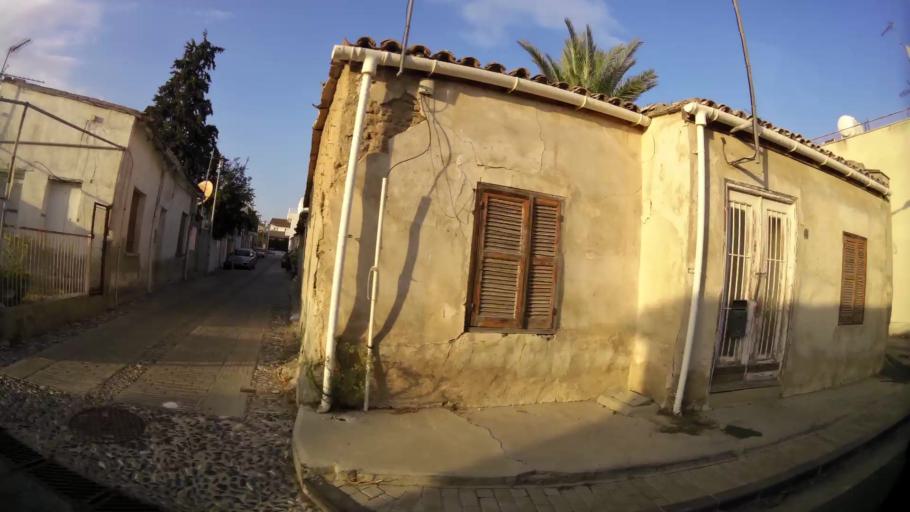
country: CY
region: Lefkosia
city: Nicosia
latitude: 35.1707
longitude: 33.3312
